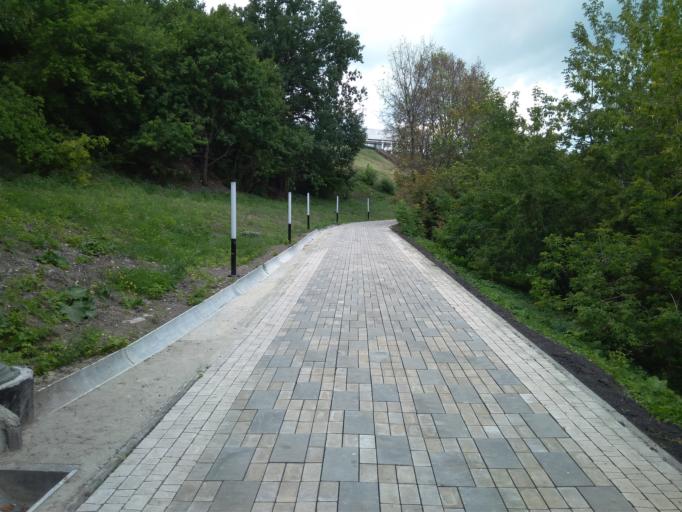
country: RU
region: Ulyanovsk
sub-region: Ulyanovskiy Rayon
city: Ulyanovsk
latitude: 54.3180
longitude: 48.4093
